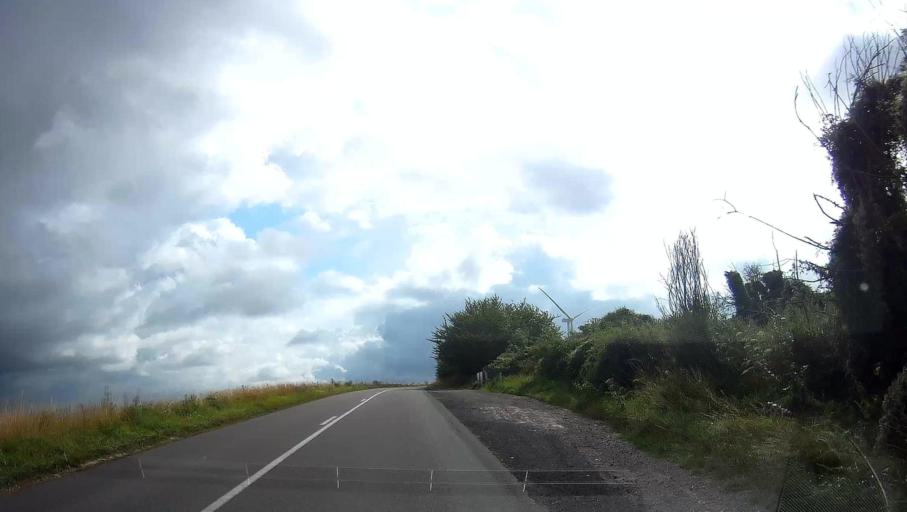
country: FR
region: Champagne-Ardenne
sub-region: Departement des Ardennes
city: Rethel
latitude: 49.5395
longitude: 4.3084
